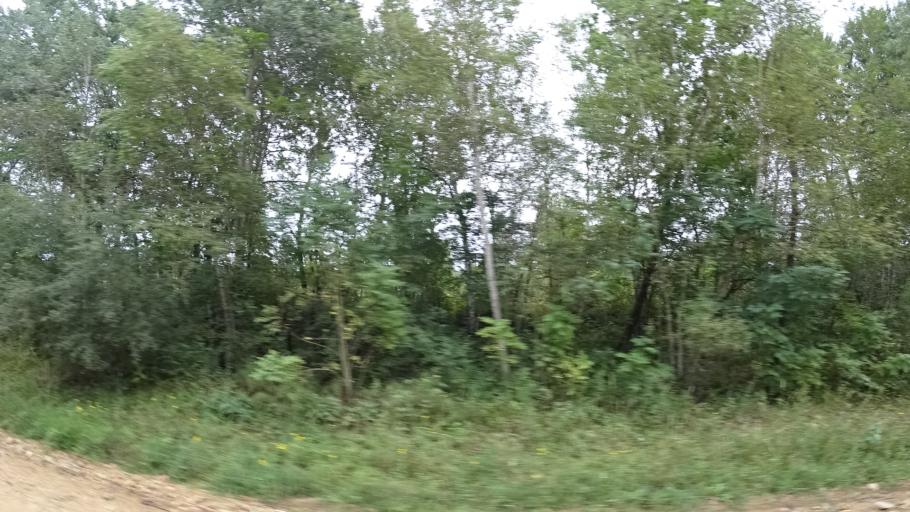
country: RU
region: Primorskiy
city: Rettikhovka
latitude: 44.1551
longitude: 132.6820
